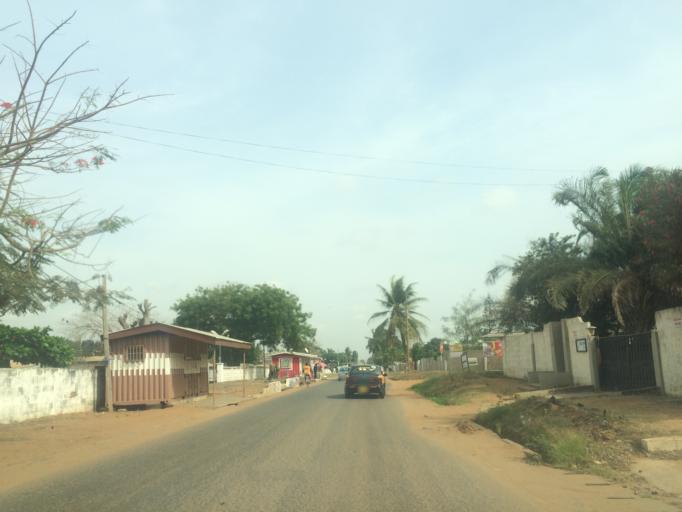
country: GH
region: Greater Accra
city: Nungua
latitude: 5.5982
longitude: -0.0904
